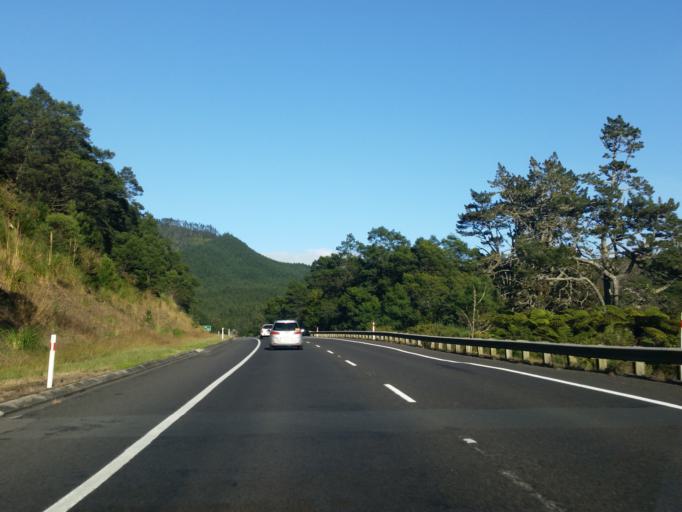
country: NZ
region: Bay of Plenty
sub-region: Western Bay of Plenty District
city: Waihi Beach
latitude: -37.4597
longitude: 175.9204
